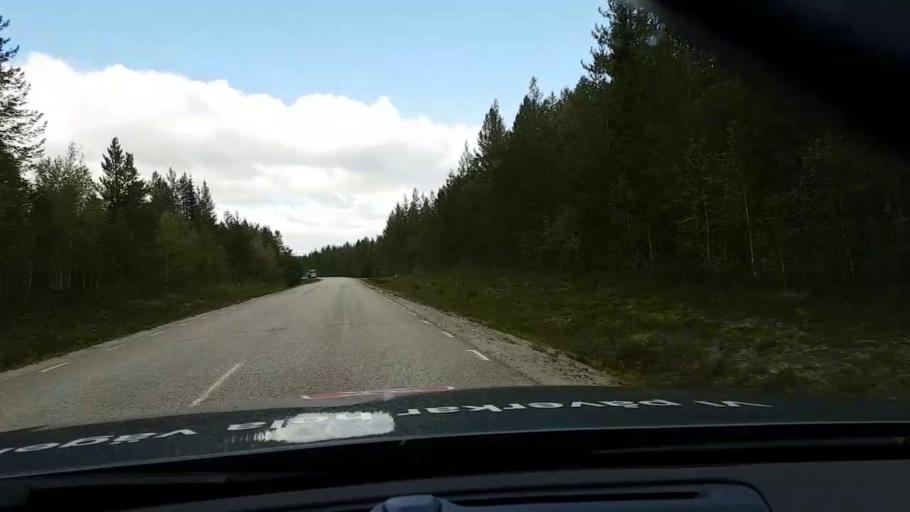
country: SE
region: Vaesterbotten
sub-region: Asele Kommun
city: Asele
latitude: 63.9237
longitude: 17.3190
